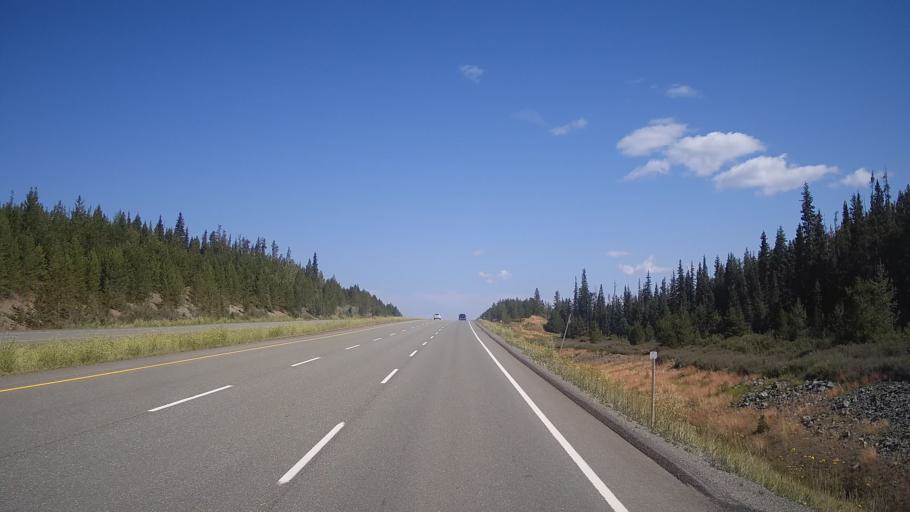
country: CA
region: British Columbia
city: Logan Lake
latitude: 50.3444
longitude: -120.6285
